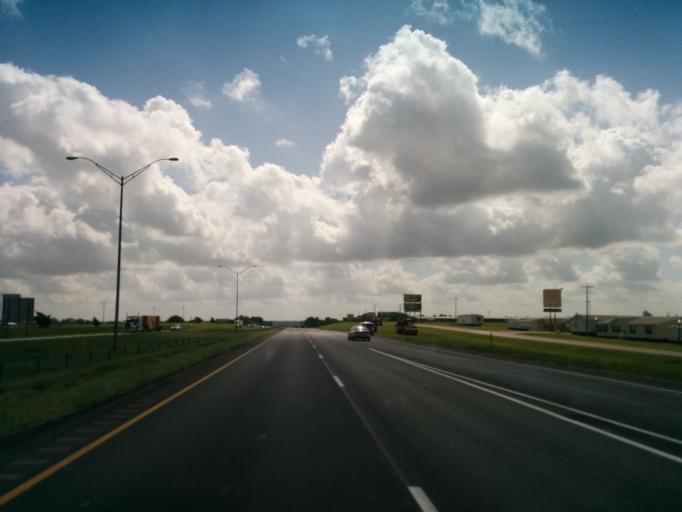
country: US
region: Texas
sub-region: Fayette County
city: Schulenburg
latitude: 29.6941
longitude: -96.8978
